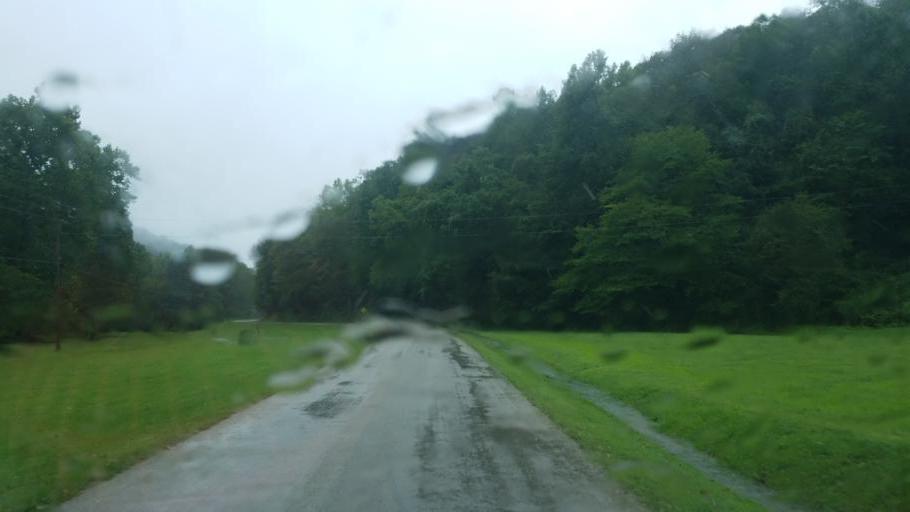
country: US
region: Kentucky
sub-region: Lewis County
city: Vanceburg
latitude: 38.8003
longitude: -83.2549
